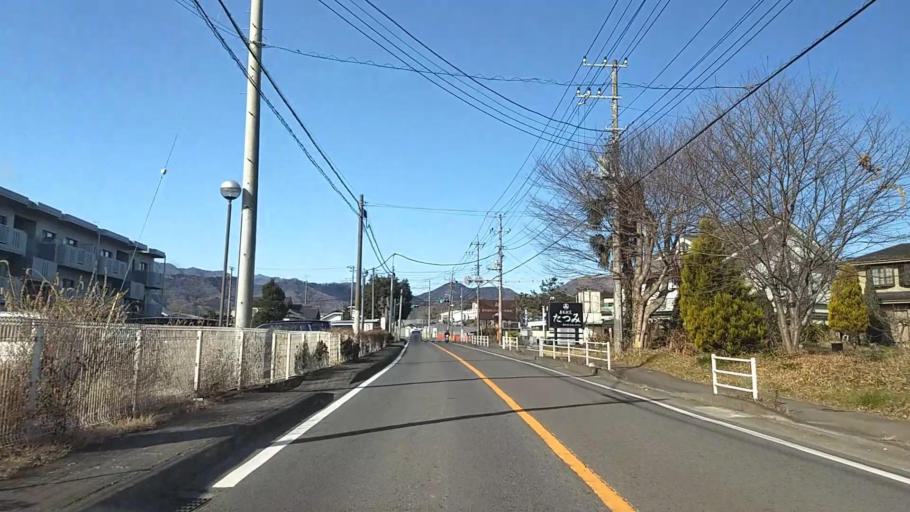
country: JP
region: Kanagawa
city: Atsugi
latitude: 35.4693
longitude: 139.3277
